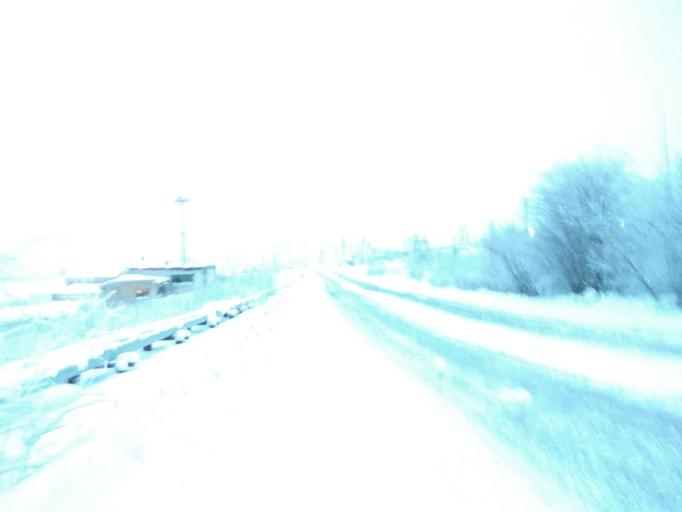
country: RU
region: Sakha
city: Aykhal
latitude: 65.9348
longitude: 111.5088
